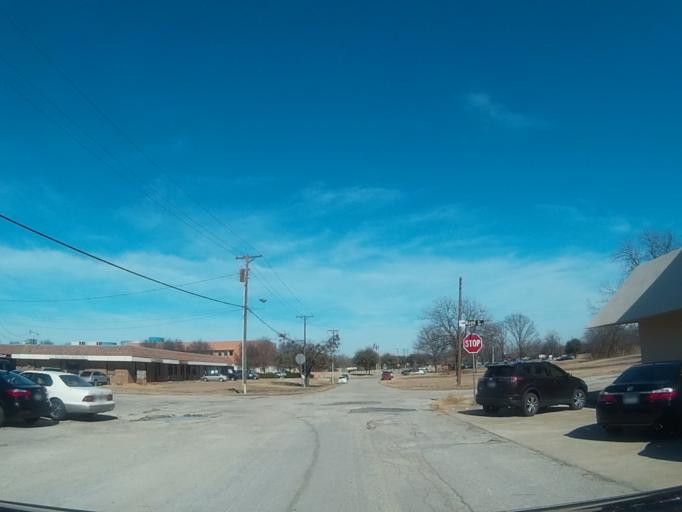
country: US
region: Texas
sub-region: Collin County
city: Allen
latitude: 33.1039
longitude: -96.6707
